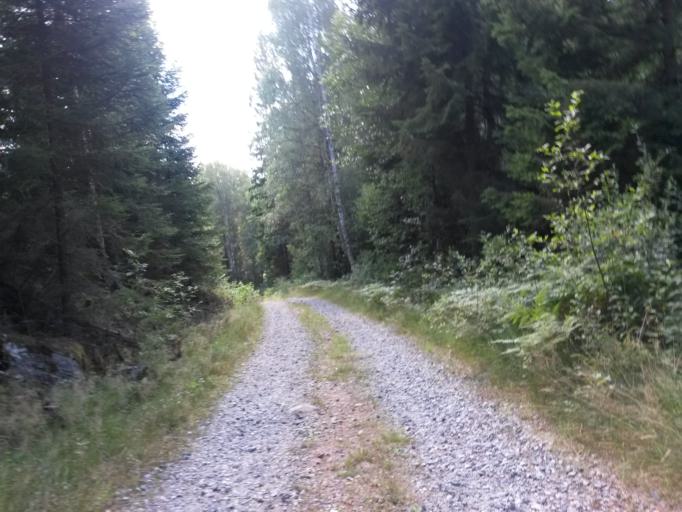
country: SE
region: Vaestra Goetaland
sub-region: Vargarda Kommun
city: Jonstorp
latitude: 57.9502
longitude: 12.6819
